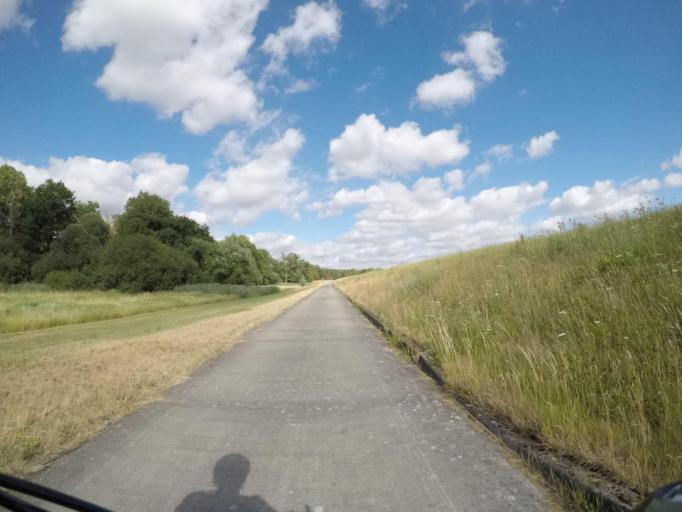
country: DE
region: Lower Saxony
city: Damnatz
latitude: 53.1666
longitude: 11.1682
